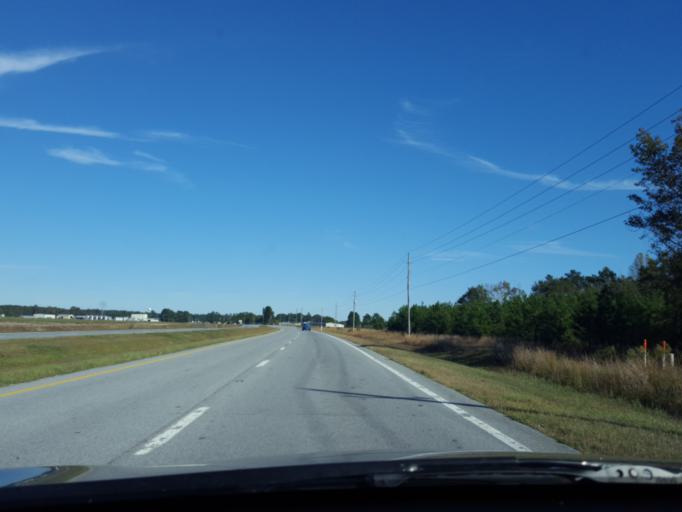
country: US
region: North Carolina
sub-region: Pitt County
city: Greenville
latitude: 35.6223
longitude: -77.2431
